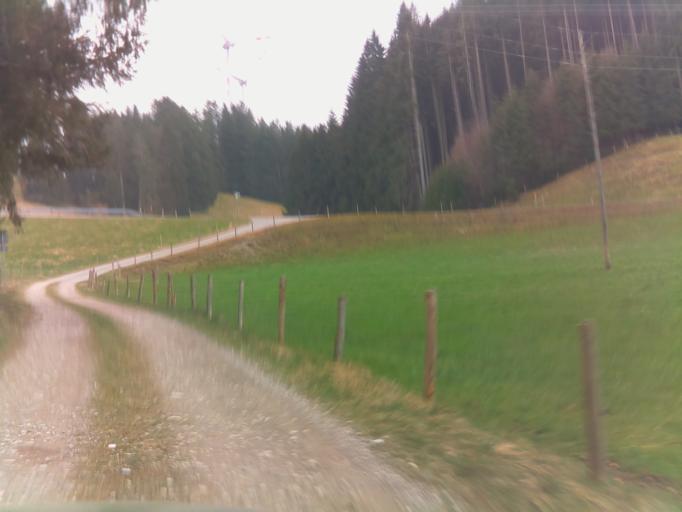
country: DE
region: Bavaria
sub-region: Swabia
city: Bidingen
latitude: 47.8308
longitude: 10.7466
